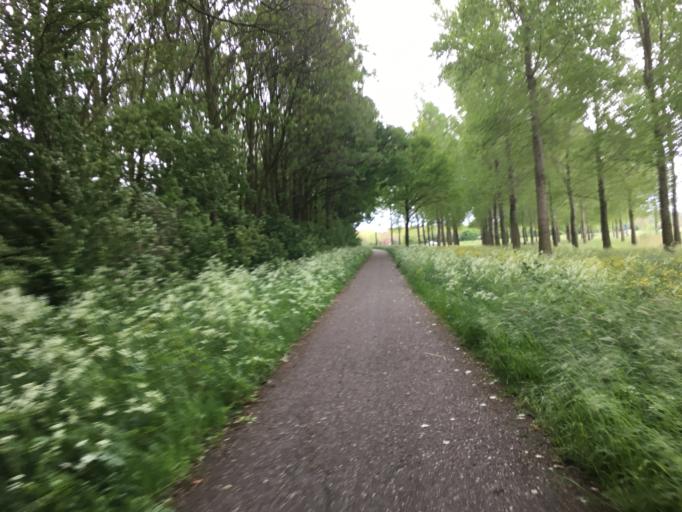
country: NL
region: Gelderland
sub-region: Gemeente Maasdriel
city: Hedel
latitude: 51.7254
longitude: 5.2450
